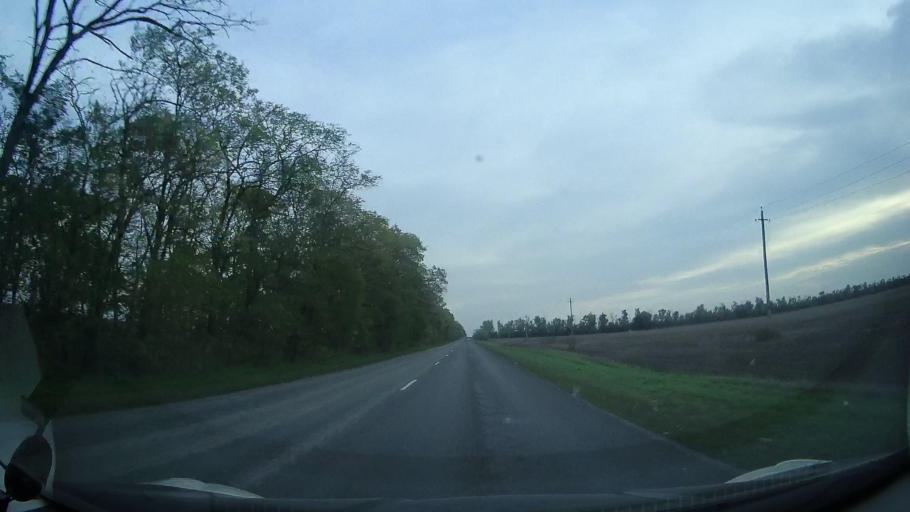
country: RU
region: Rostov
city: Ol'ginskaya
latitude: 47.1023
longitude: 39.9776
